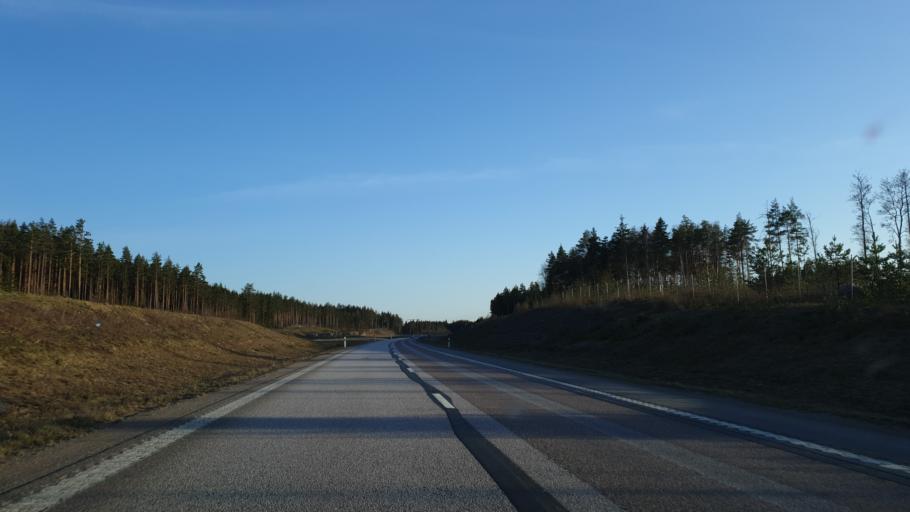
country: SE
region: Uppsala
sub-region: Tierps Kommun
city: Tierp
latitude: 60.3061
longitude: 17.5212
